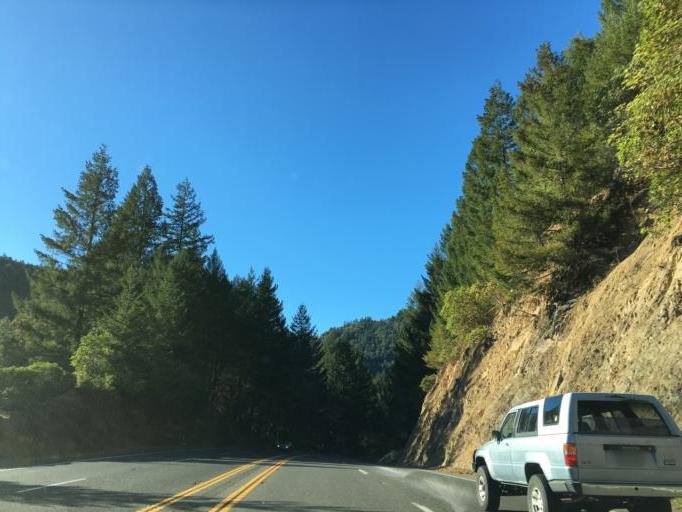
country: US
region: California
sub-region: Mendocino County
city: Brooktrails
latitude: 39.5229
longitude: -123.3958
